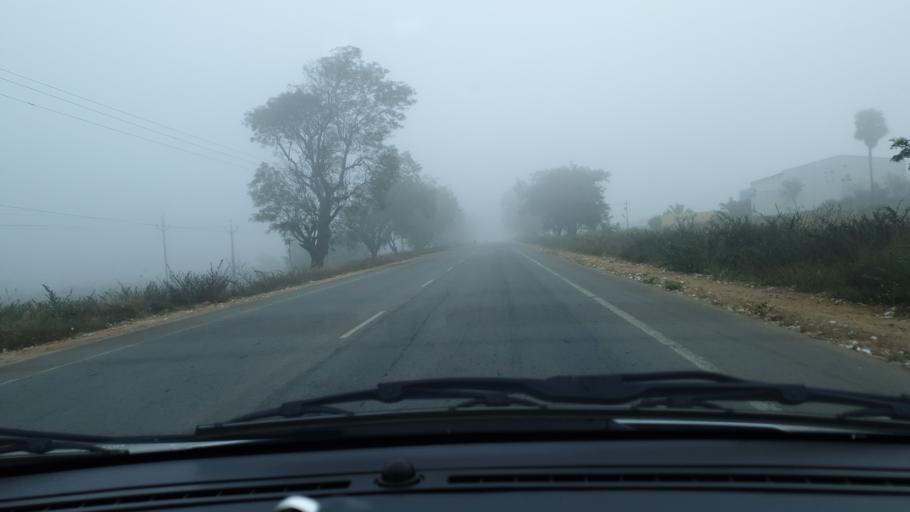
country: IN
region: Telangana
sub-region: Mahbubnagar
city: Nagar Karnul
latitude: 16.6646
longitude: 78.5524
